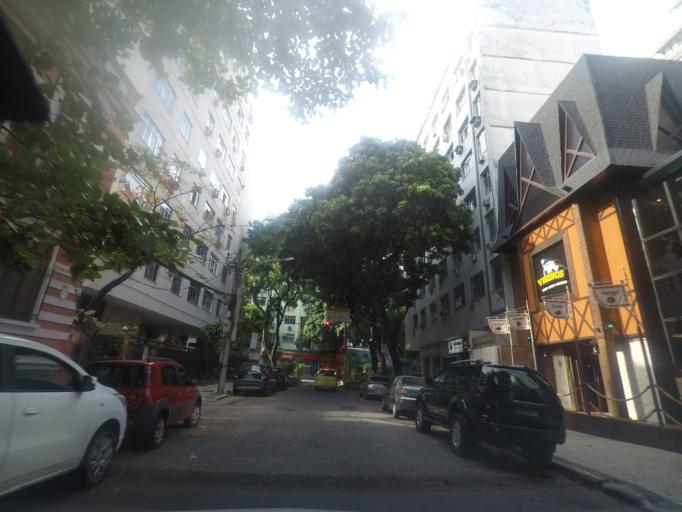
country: BR
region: Rio de Janeiro
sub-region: Rio De Janeiro
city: Rio de Janeiro
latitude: -22.9565
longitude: -43.1972
